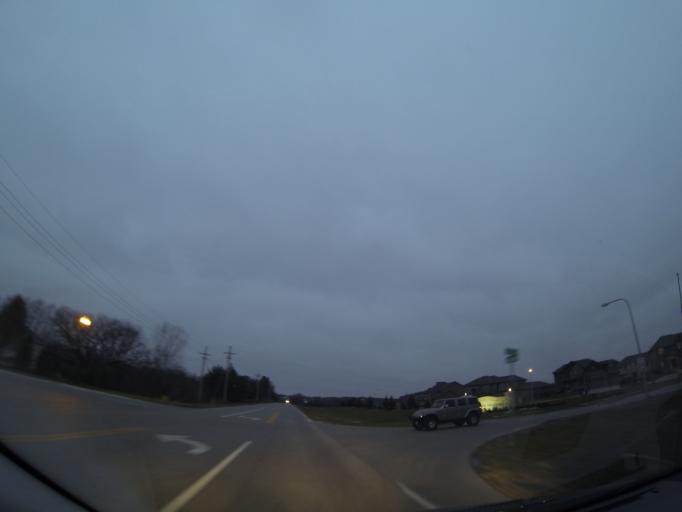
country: US
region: Nebraska
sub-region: Douglas County
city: Elkhorn
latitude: 41.2776
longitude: -96.1914
